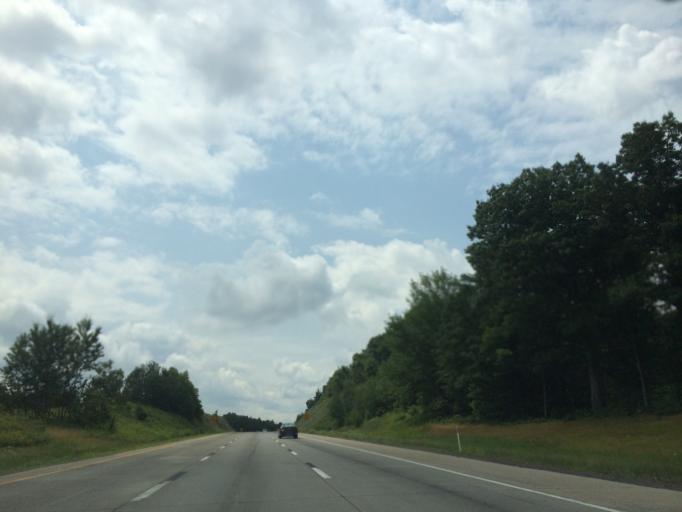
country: US
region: Pennsylvania
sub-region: Luzerne County
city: Harleigh
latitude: 41.0657
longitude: -75.9874
